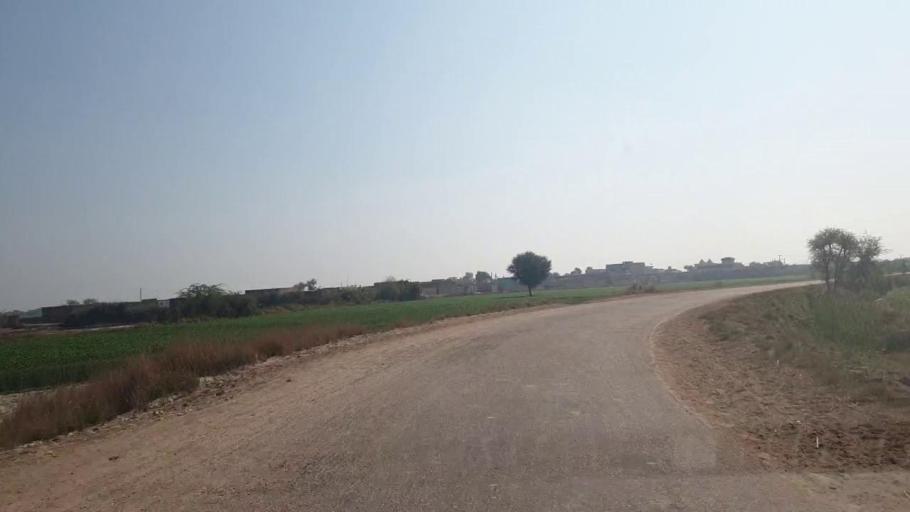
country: PK
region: Sindh
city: Sakrand
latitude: 26.0487
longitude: 68.4211
